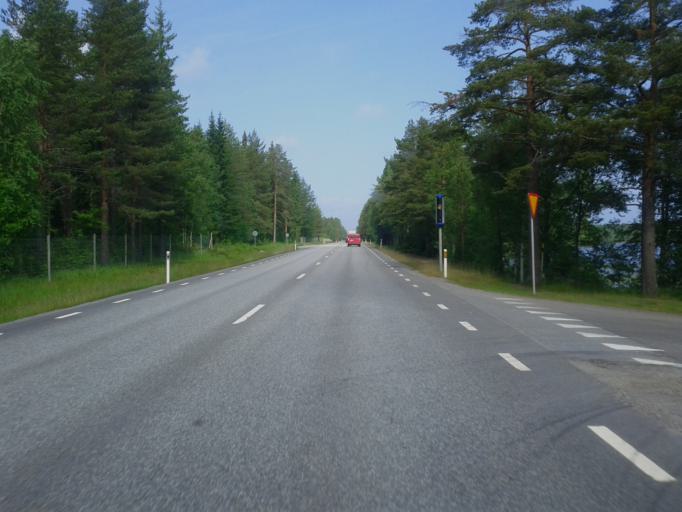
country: SE
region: Vaesterbotten
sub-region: Skelleftea Kommun
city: Burea
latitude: 64.5394
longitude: 21.2558
